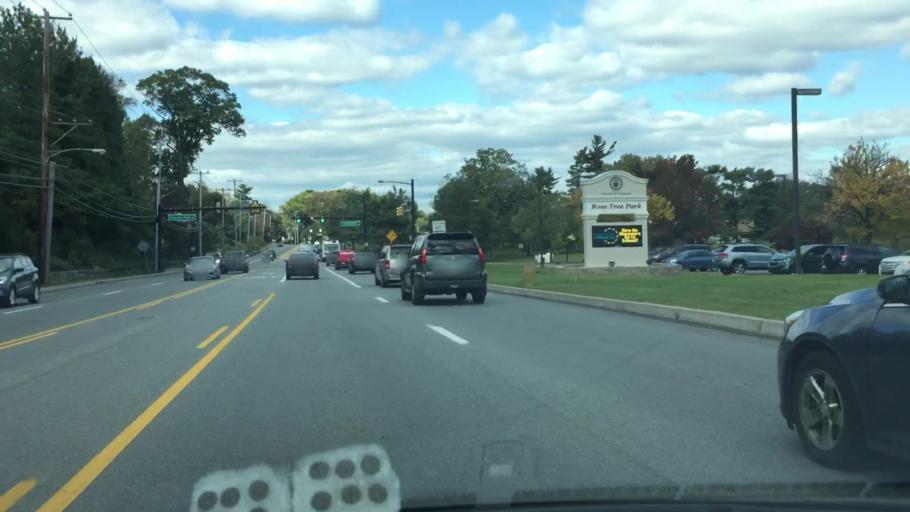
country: US
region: Pennsylvania
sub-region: Delaware County
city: Media
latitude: 39.9393
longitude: -75.3944
